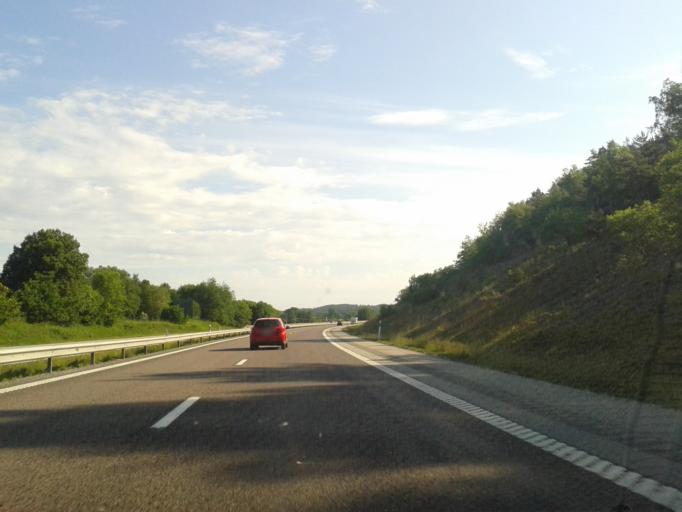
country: SE
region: Vaestra Goetaland
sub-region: Stenungsunds Kommun
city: Stora Hoga
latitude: 58.0411
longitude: 11.8472
